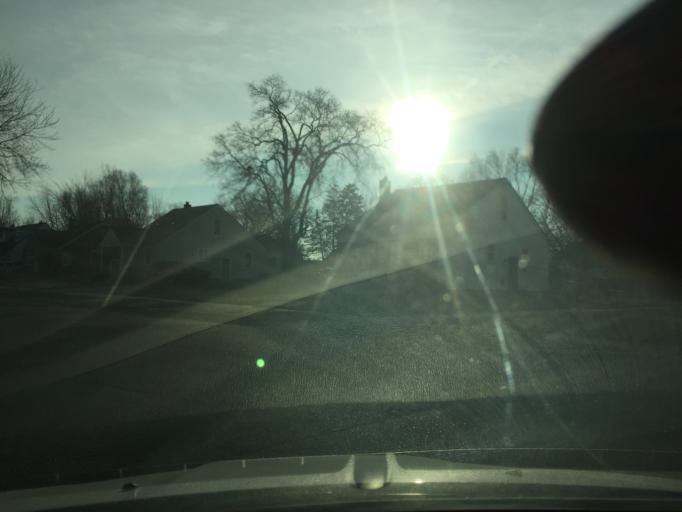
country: US
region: Michigan
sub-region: Macomb County
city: Eastpointe
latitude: 42.4417
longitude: -82.9657
